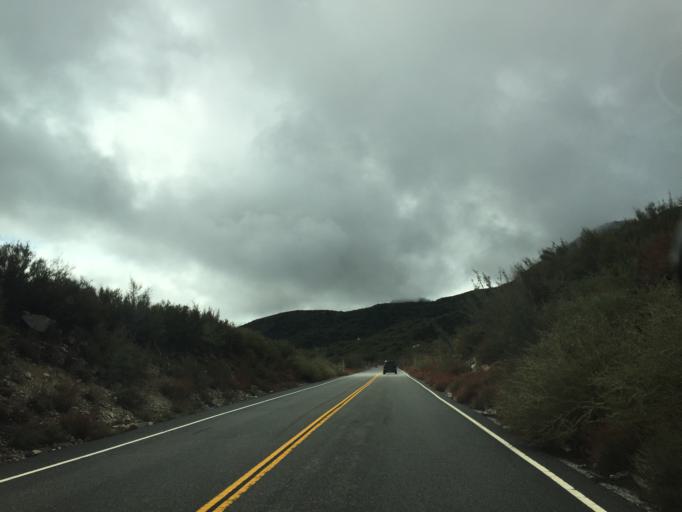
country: US
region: California
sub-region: Los Angeles County
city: Glendora
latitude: 34.3084
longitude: -117.8445
